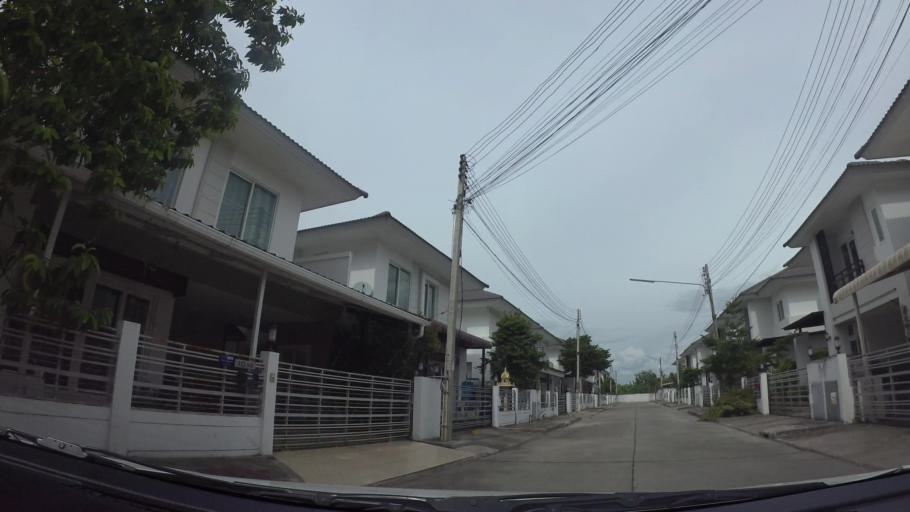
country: TH
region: Chiang Mai
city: Chiang Mai
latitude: 18.7460
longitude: 98.9661
